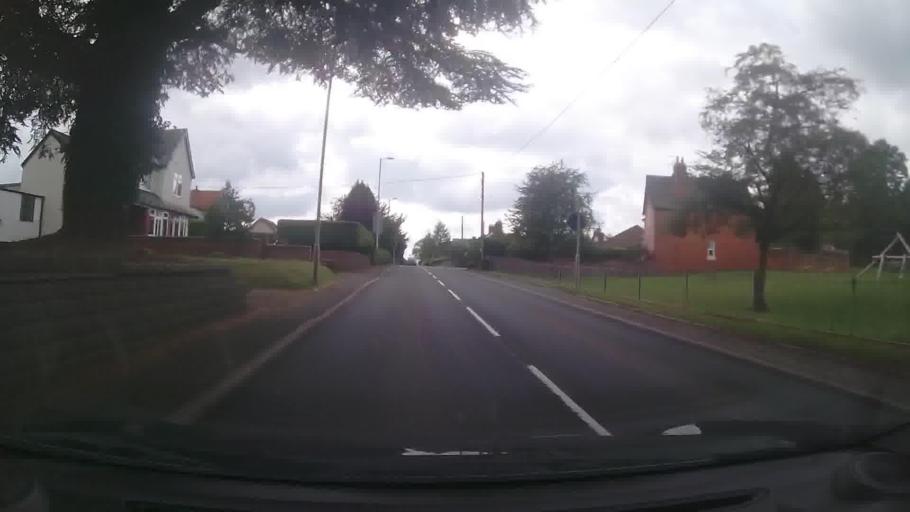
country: GB
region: England
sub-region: Shropshire
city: Pant
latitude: 52.7902
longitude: -3.0798
